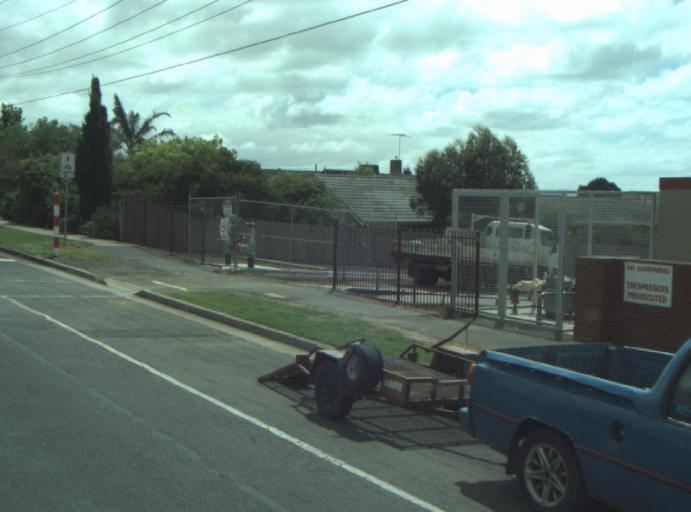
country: AU
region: Victoria
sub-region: Greater Geelong
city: Wandana Heights
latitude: -38.1853
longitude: 144.3104
